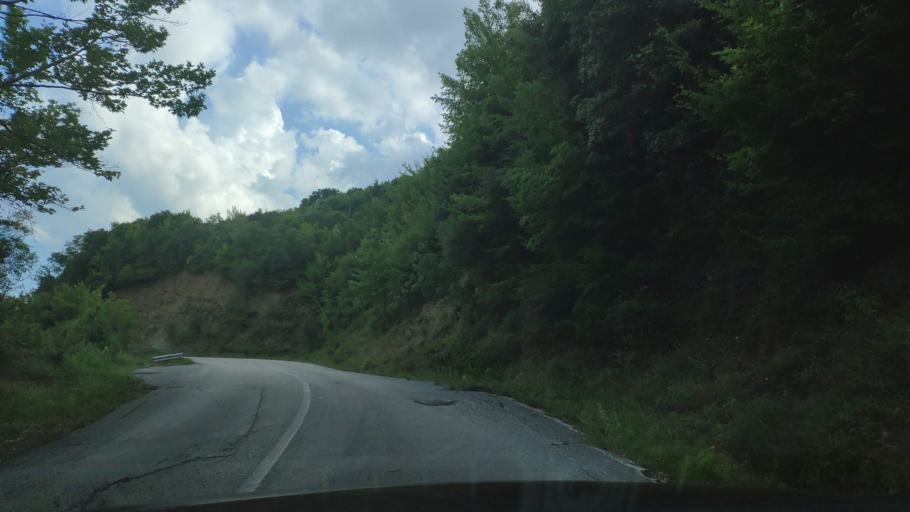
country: GR
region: Epirus
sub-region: Nomos Artas
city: Agios Dimitrios
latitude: 39.4559
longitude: 21.0235
